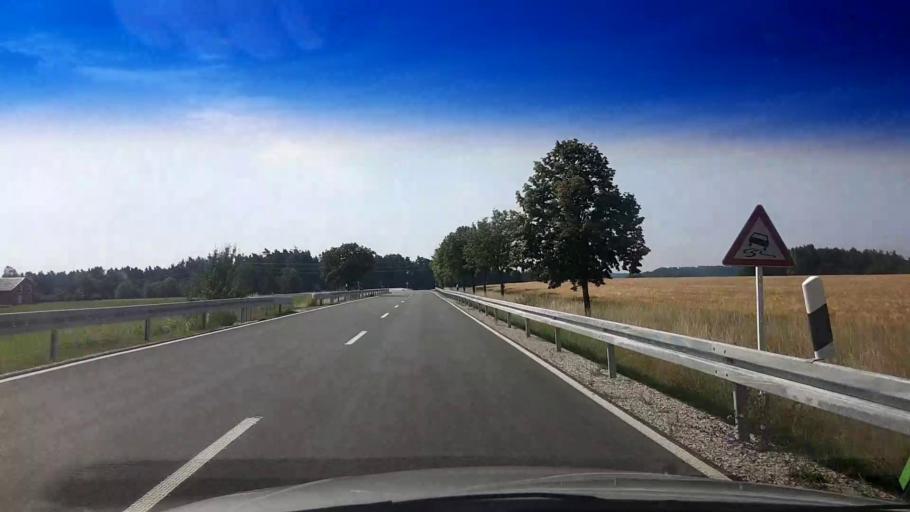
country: DE
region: Bavaria
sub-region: Upper Franconia
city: Mistelgau
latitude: 49.9417
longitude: 11.4501
